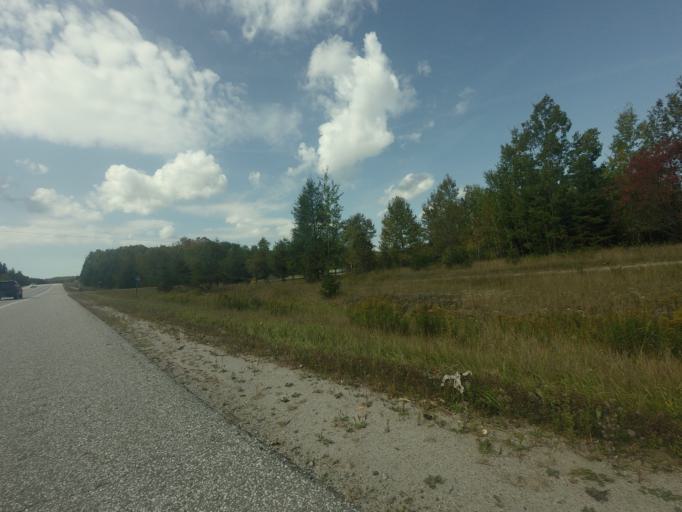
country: CA
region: Quebec
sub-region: Laurentides
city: Mont-Laurier
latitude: 46.5597
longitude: -75.6373
